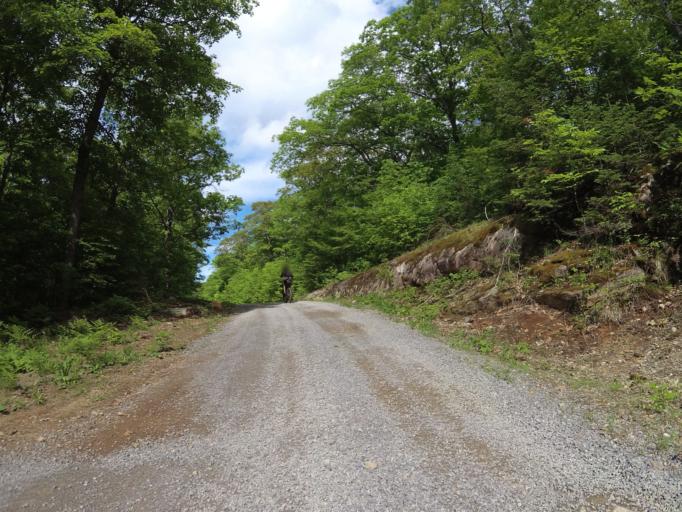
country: CA
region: Ontario
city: Renfrew
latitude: 45.1200
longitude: -76.8844
